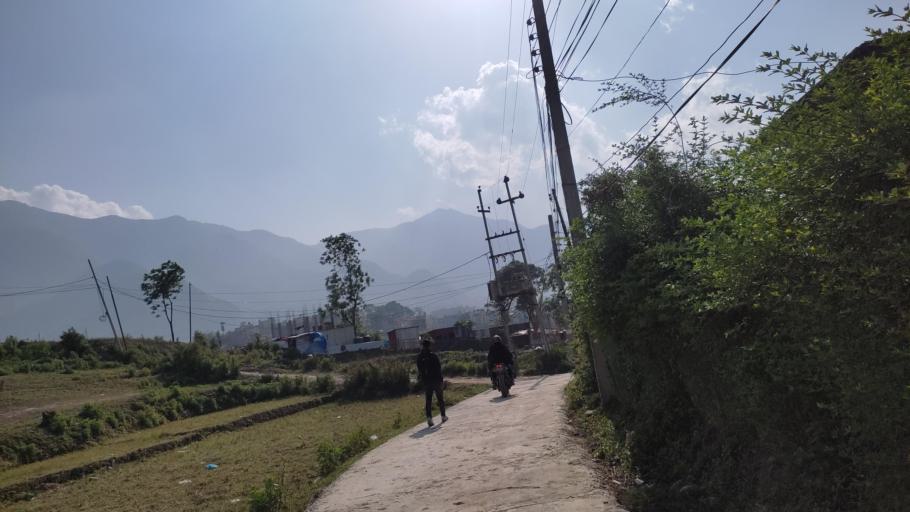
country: NP
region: Central Region
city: Kirtipur
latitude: 27.6782
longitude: 85.2655
